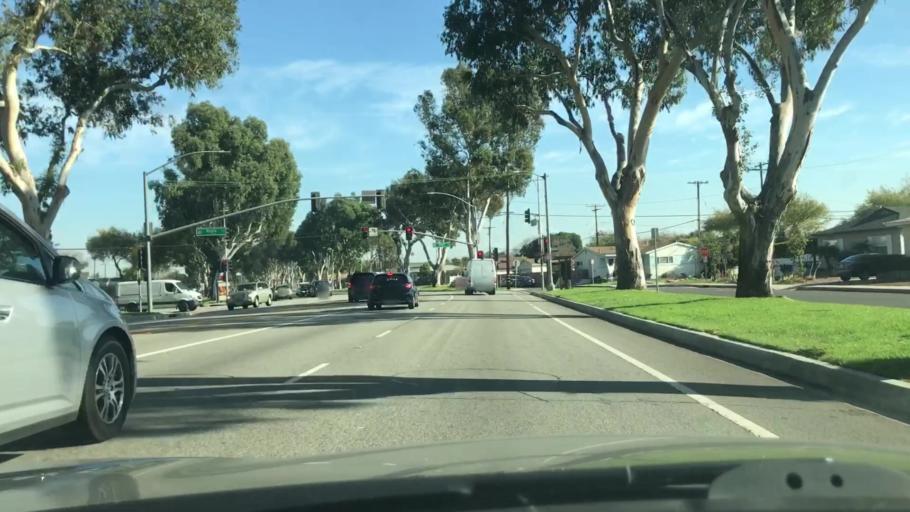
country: US
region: California
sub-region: Los Angeles County
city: Torrance
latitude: 33.8364
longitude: -118.3408
